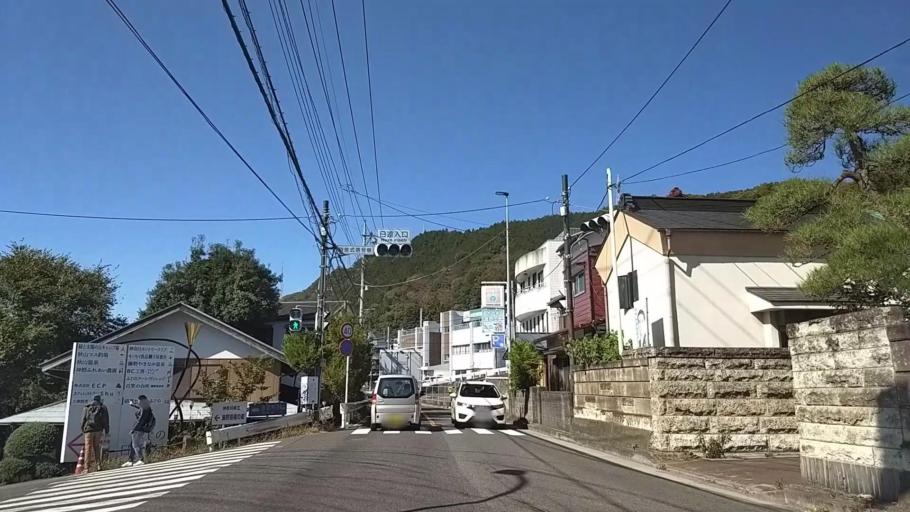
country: JP
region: Yamanashi
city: Uenohara
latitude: 35.6148
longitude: 139.1543
